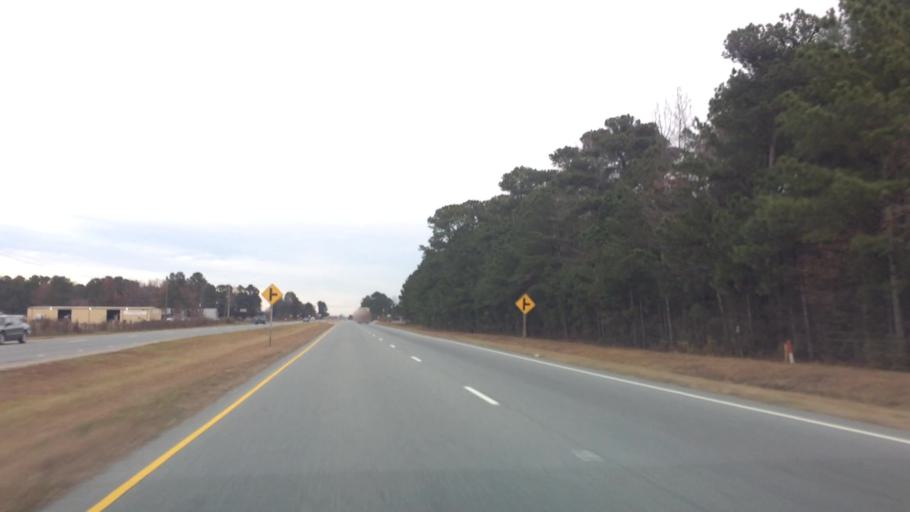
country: US
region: North Carolina
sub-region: Wayne County
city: Mount Olive
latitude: 35.1681
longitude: -78.1038
